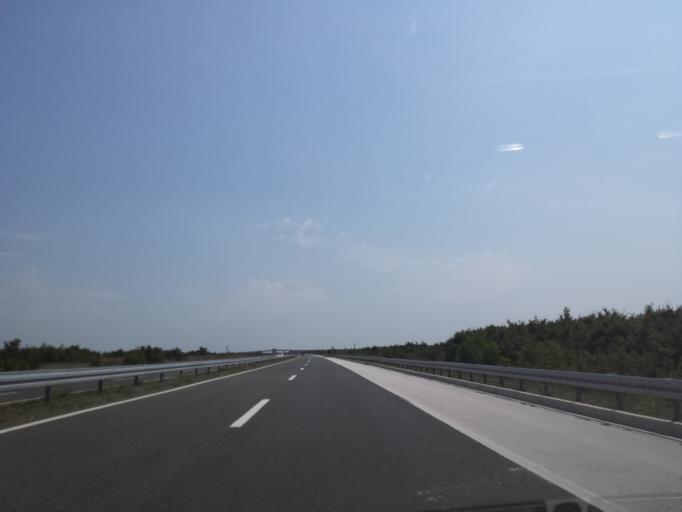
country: HR
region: Sibensko-Kniniska
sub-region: Grad Sibenik
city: Pirovac
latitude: 43.9332
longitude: 15.7113
